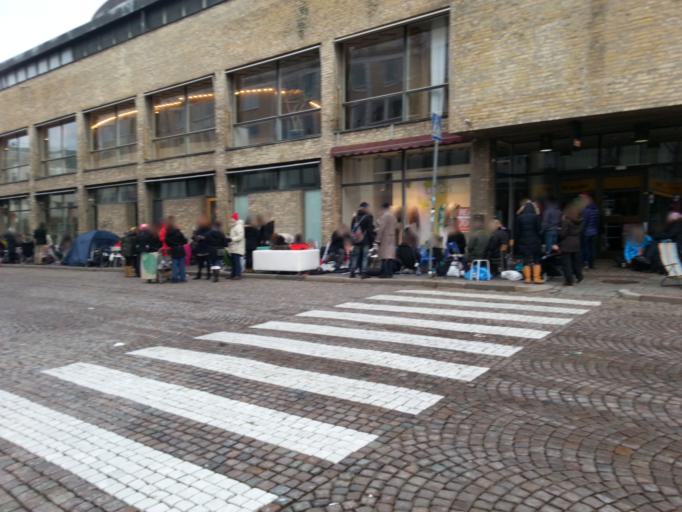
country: SE
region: Skane
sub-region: Lunds Kommun
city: Lund
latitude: 55.7022
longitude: 13.1938
